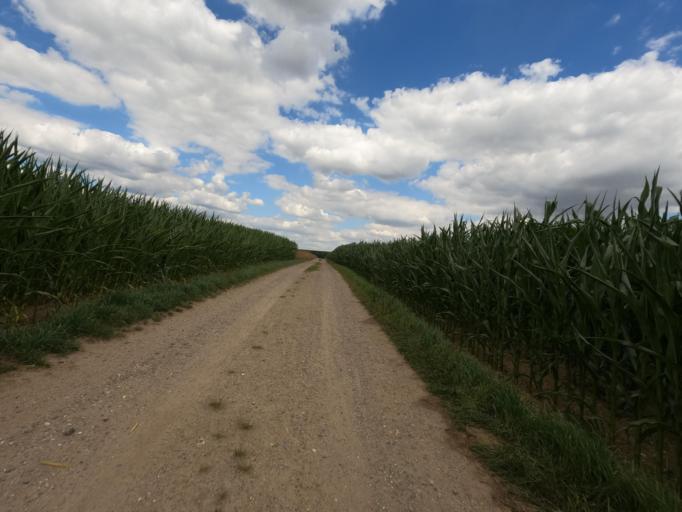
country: DE
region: North Rhine-Westphalia
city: Geilenkirchen
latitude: 50.9971
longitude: 6.1337
